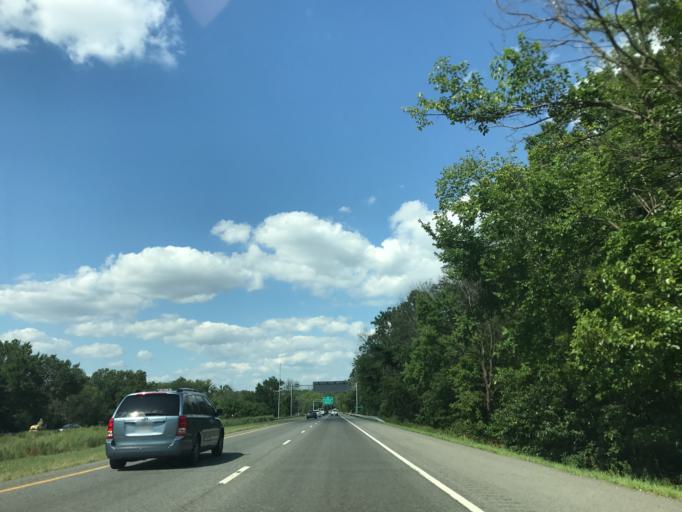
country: US
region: Maryland
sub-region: Howard County
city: Hanover
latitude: 39.1857
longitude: -76.7168
